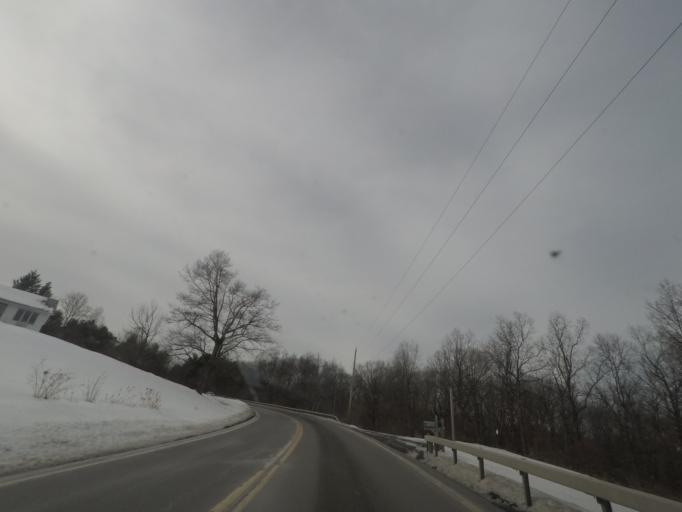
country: US
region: New York
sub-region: Albany County
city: Altamont
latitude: 42.6973
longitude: -74.0525
